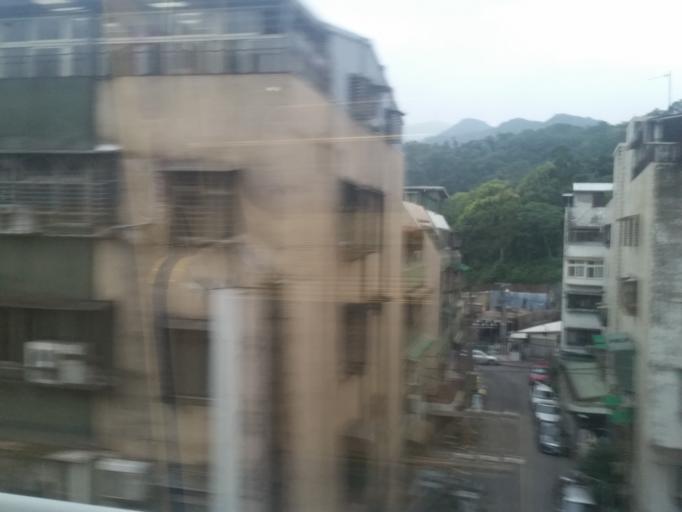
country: TW
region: Taipei
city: Taipei
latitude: 25.0844
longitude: 121.5960
